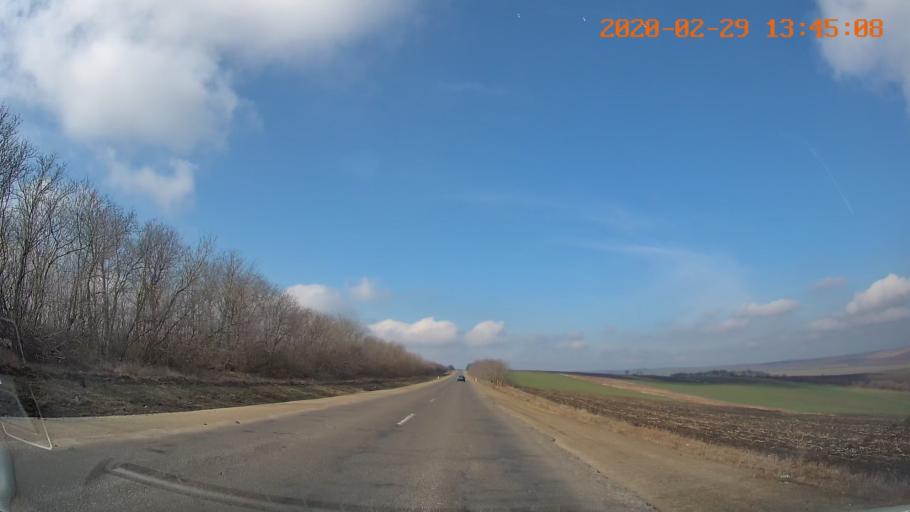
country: MD
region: Floresti
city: Leninskiy
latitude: 47.8449
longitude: 28.5174
